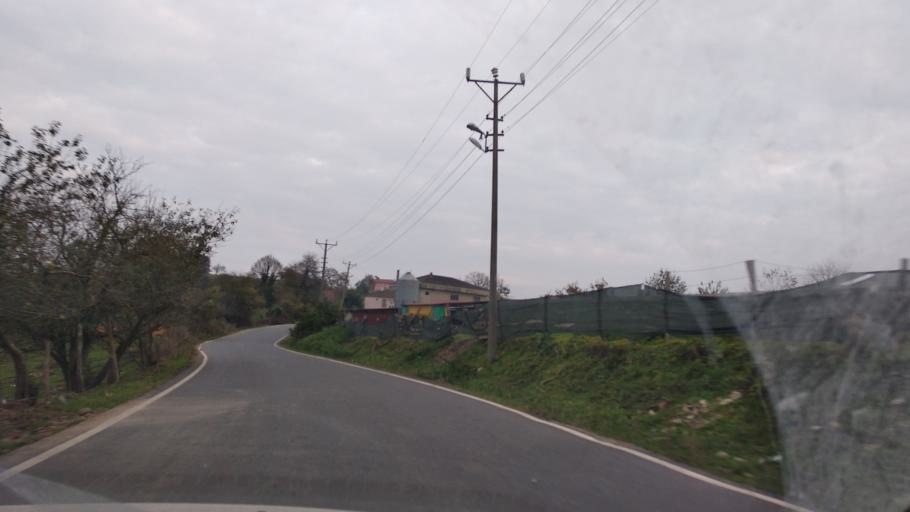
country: TR
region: Sakarya
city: Ortakoy
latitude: 41.0347
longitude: 30.6600
